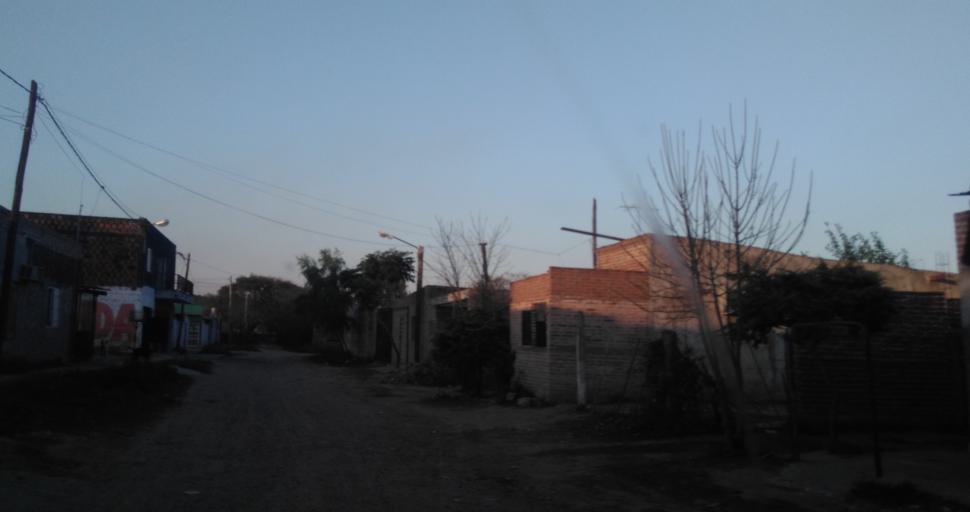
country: AR
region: Chaco
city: Fontana
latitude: -27.4282
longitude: -59.0003
